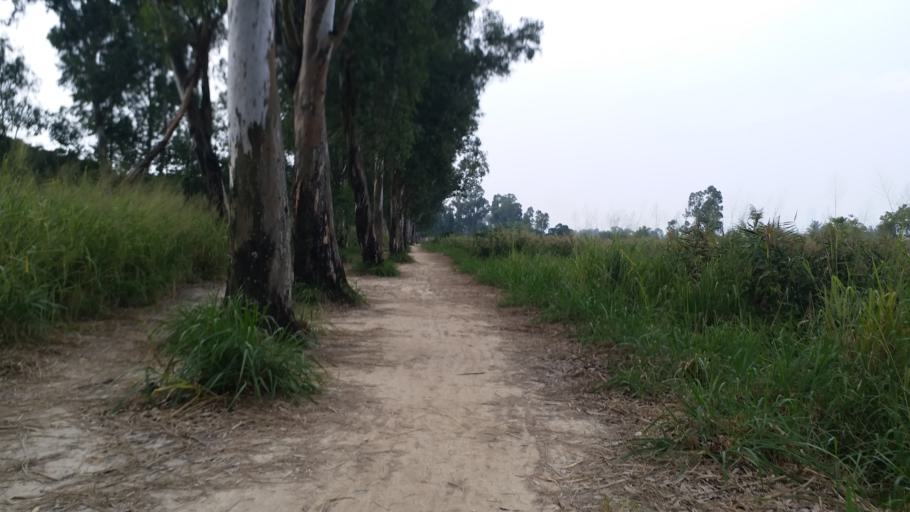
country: HK
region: Yuen Long
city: Yuen Long Kau Hui
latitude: 22.4561
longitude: 114.0346
